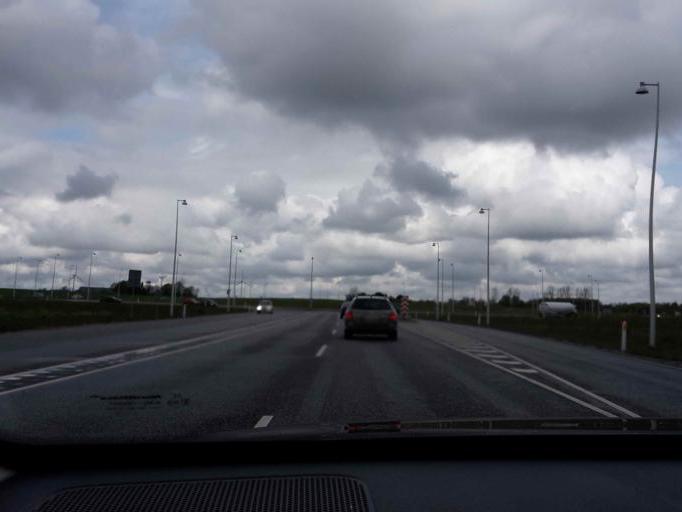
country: DK
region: South Denmark
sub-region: Vejle Kommune
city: Jelling
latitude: 55.6969
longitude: 9.3789
